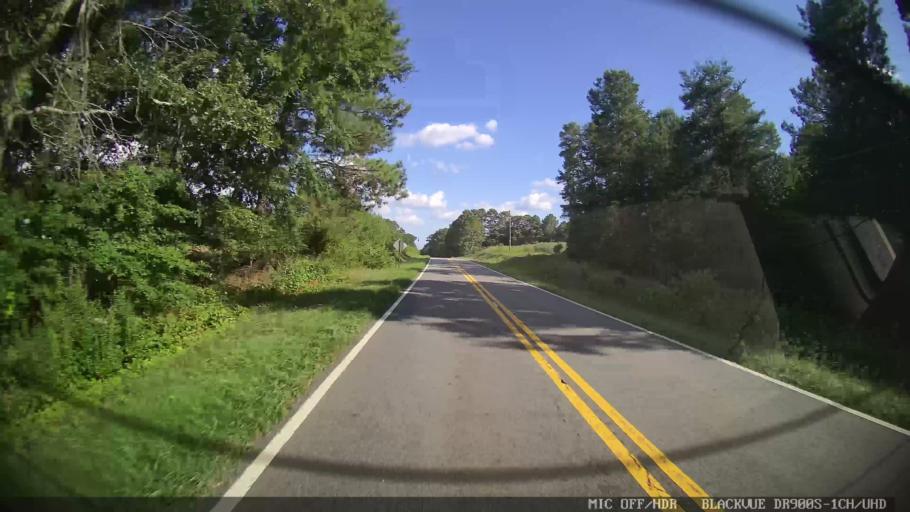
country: US
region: Georgia
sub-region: Bartow County
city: Euharlee
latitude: 34.1509
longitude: -84.9824
